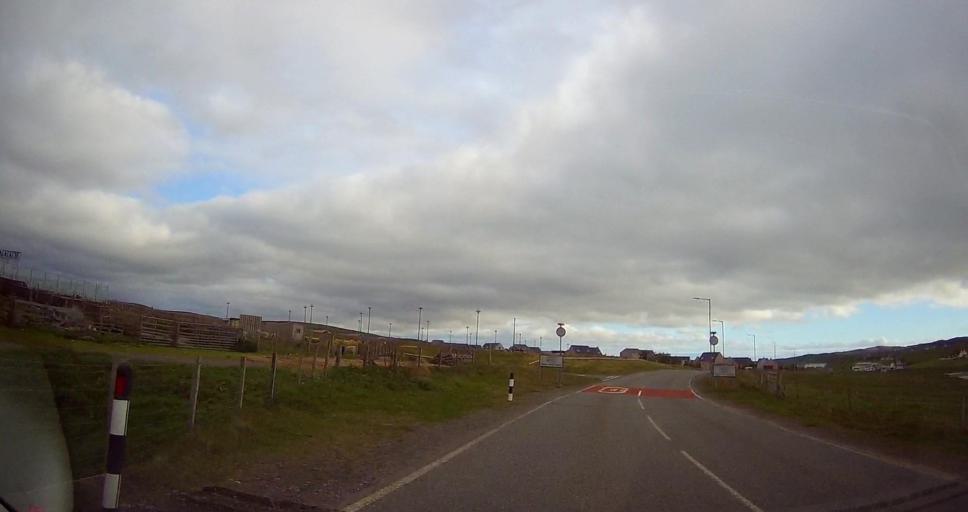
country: GB
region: Scotland
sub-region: Shetland Islands
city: Lerwick
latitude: 60.4023
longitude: -1.3493
